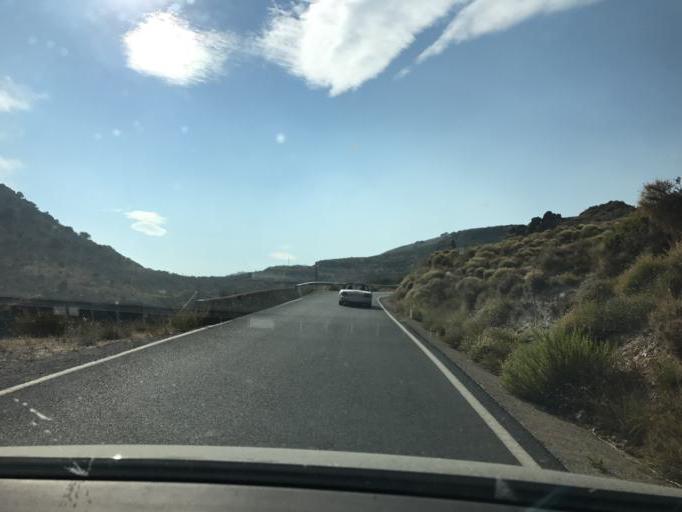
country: ES
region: Andalusia
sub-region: Provincia de Granada
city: Juviles
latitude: 36.9461
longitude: -3.2313
